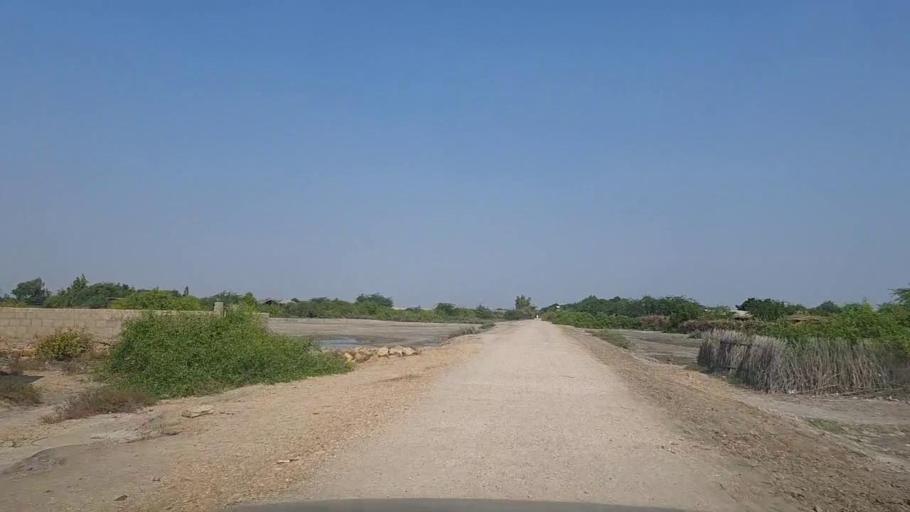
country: PK
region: Sindh
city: Thatta
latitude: 24.6151
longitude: 67.9584
